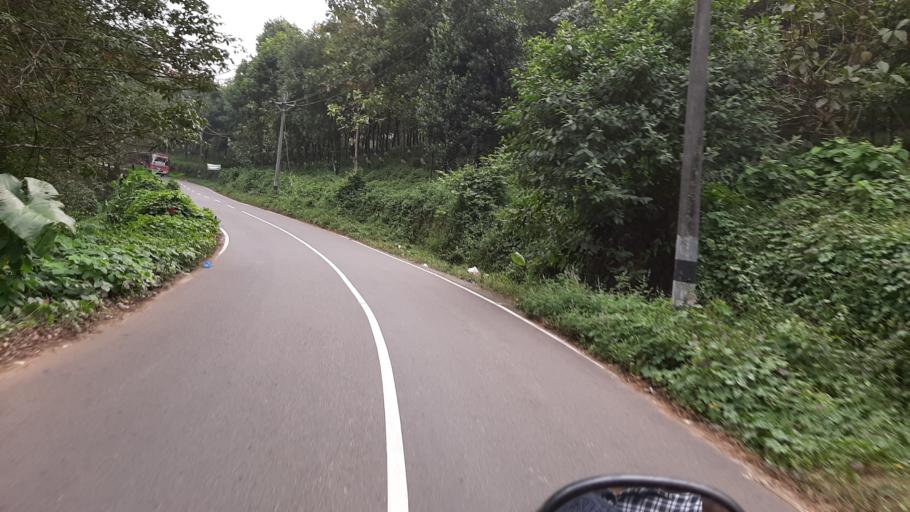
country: IN
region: Kerala
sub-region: Pattanamtitta
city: Pathanamthitta
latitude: 9.4610
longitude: 76.8696
